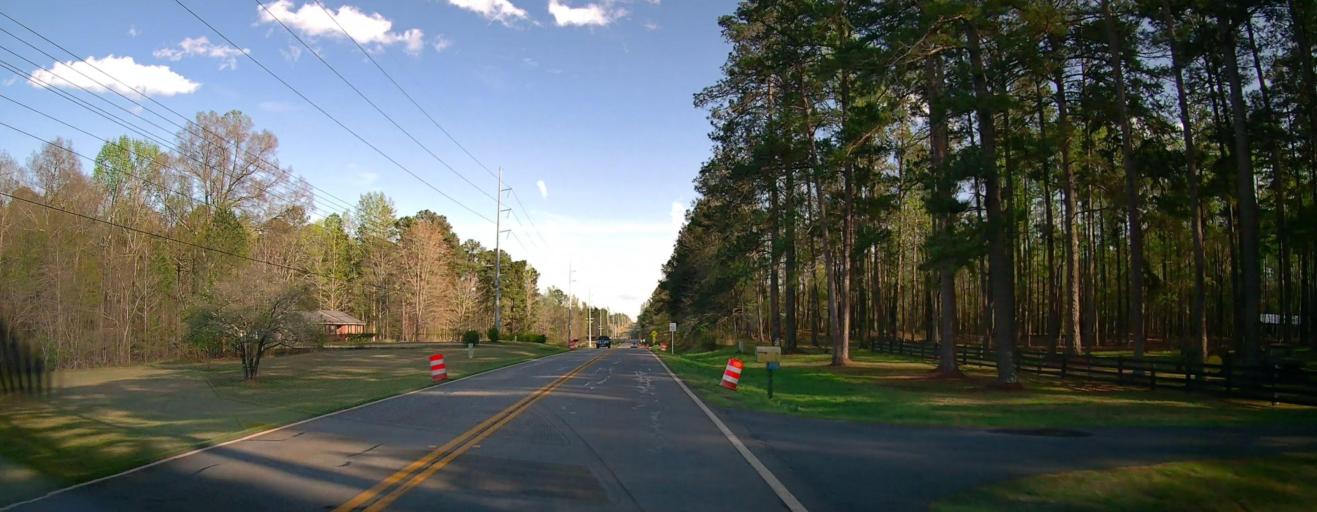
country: US
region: Georgia
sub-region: Baldwin County
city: Milledgeville
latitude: 33.1526
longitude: -83.3459
